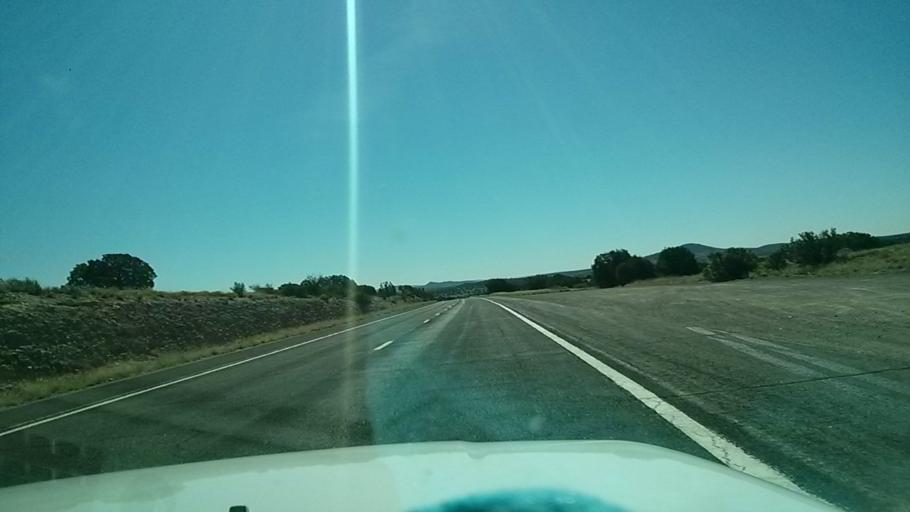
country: US
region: Arizona
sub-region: Mohave County
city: Peach Springs
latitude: 35.5523
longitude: -113.3610
